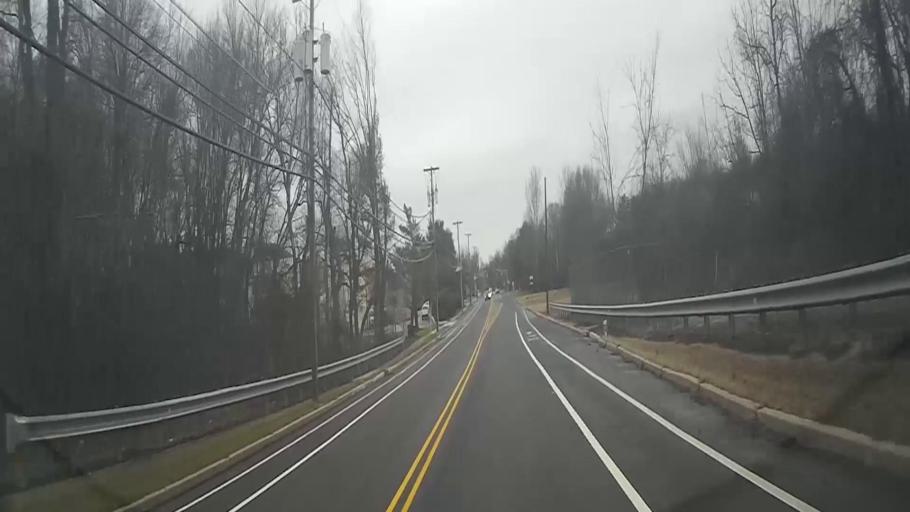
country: US
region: New Jersey
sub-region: Burlington County
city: Marlton
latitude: 39.8658
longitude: -74.9396
